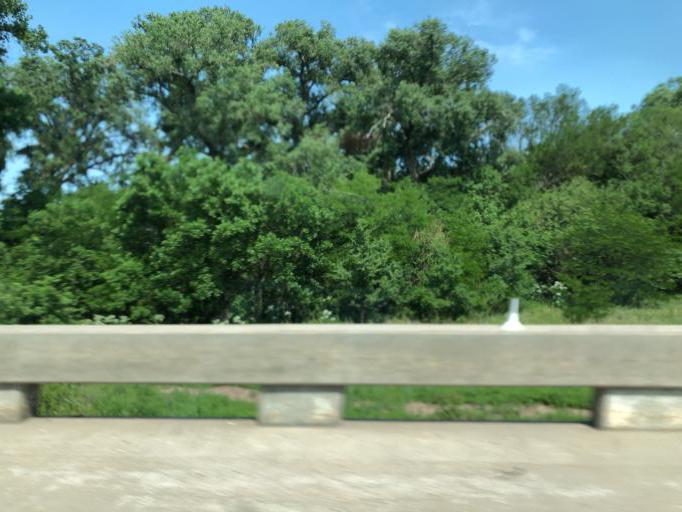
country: US
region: Nebraska
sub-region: Thayer County
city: Hebron
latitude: 40.1590
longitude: -97.5706
